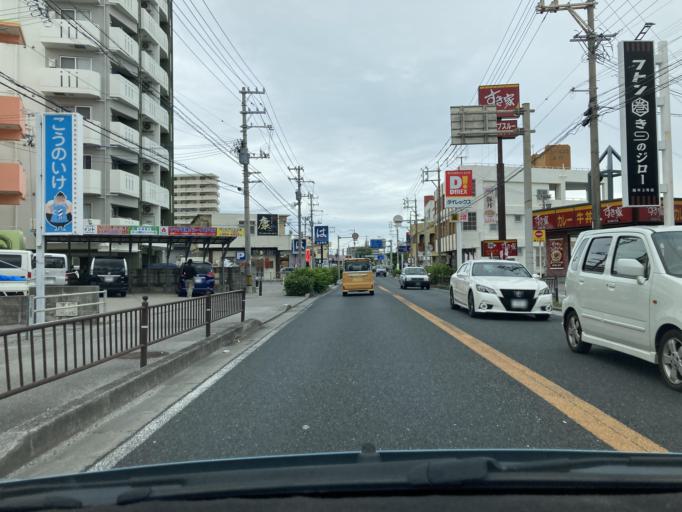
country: JP
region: Okinawa
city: Itoman
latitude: 26.1438
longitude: 127.6729
